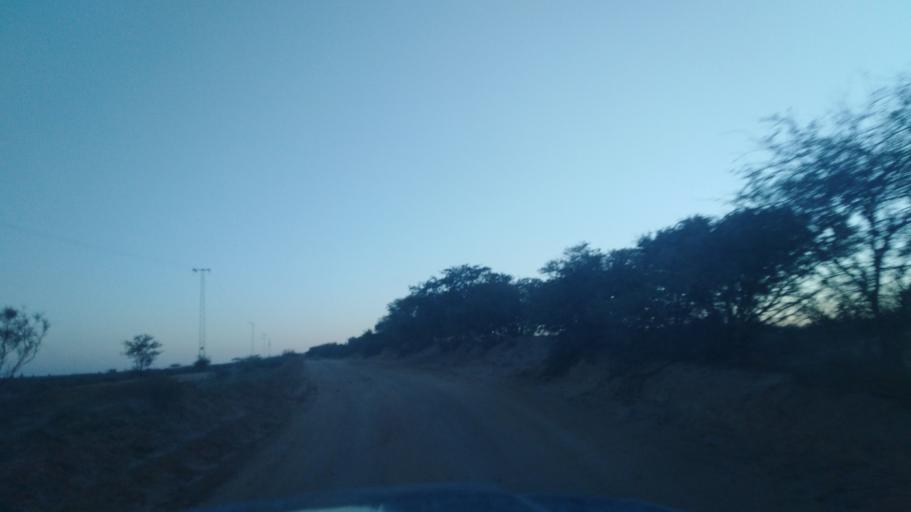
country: TN
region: Safaqis
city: Sfax
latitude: 34.7341
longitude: 10.4448
